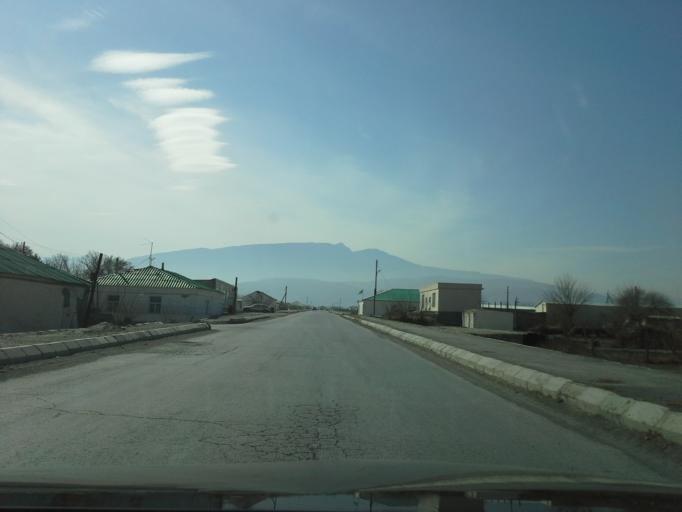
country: TM
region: Ahal
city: Abadan
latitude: 38.1099
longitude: 58.0326
